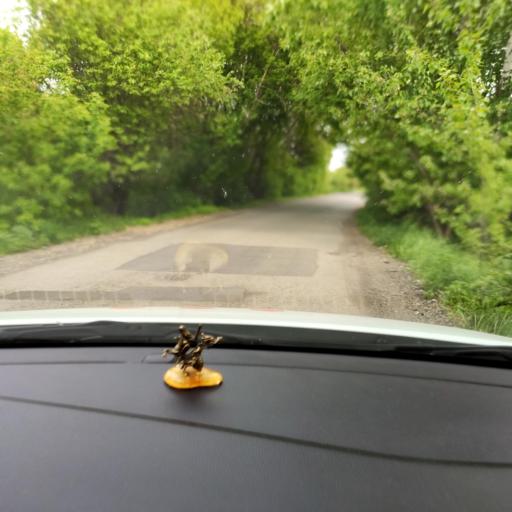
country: RU
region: Tatarstan
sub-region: Gorod Kazan'
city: Kazan
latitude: 55.7012
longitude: 49.0656
